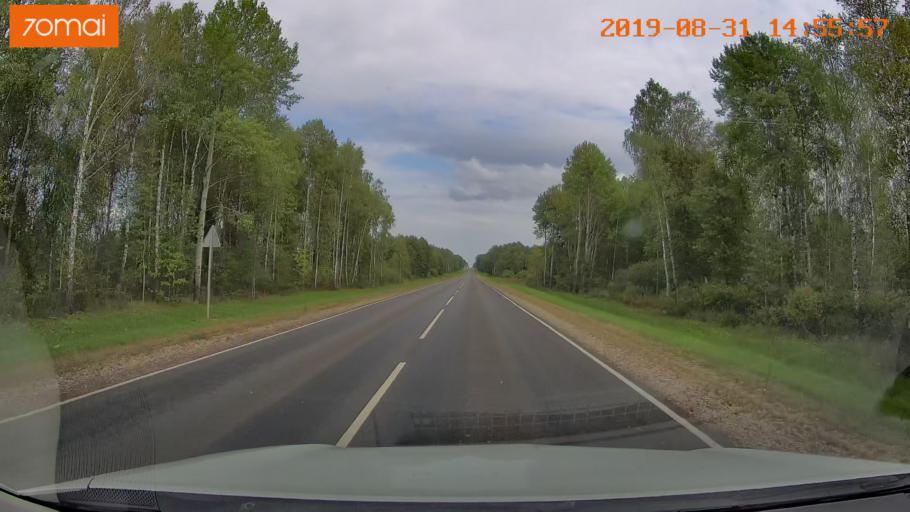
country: RU
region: Kaluga
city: Spas-Demensk
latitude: 54.3016
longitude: 33.9271
